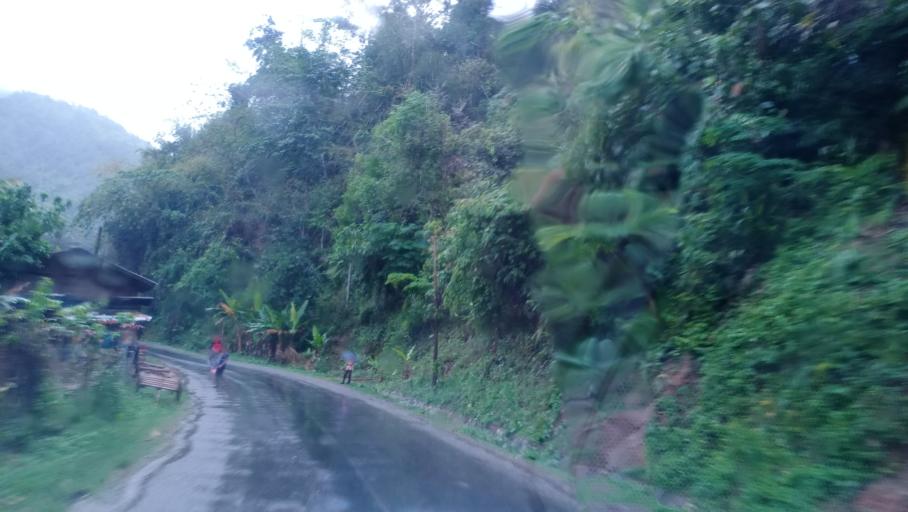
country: LA
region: Phongsali
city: Khoa
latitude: 21.0599
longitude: 102.4644
